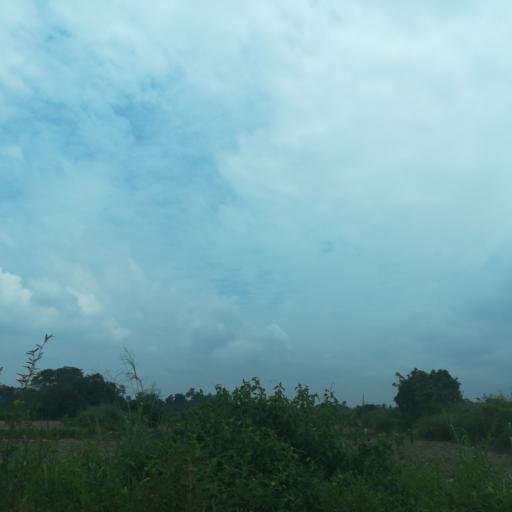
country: NG
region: Lagos
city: Ejirin
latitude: 6.6711
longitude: 3.7991
